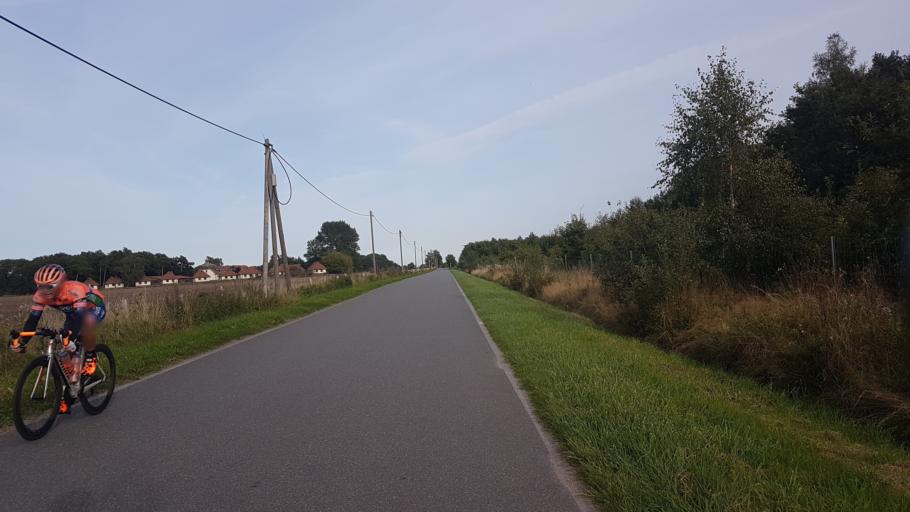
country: DE
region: Mecklenburg-Vorpommern
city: Gingst
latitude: 54.4754
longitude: 13.1605
